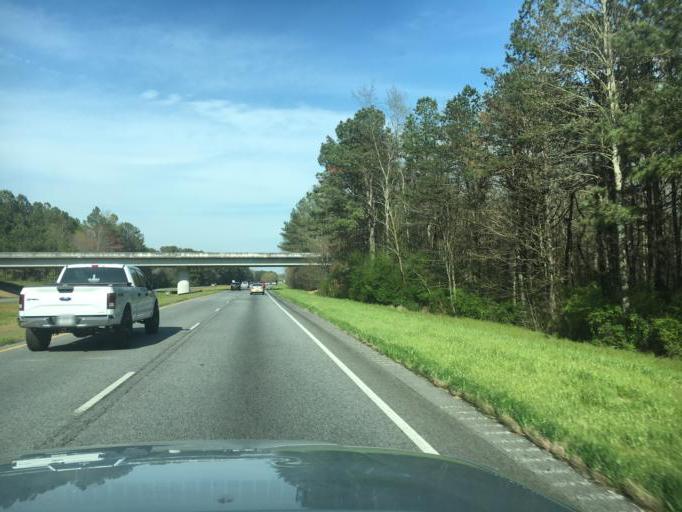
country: US
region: Georgia
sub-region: Habersham County
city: Cornelia
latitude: 34.5140
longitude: -83.5555
